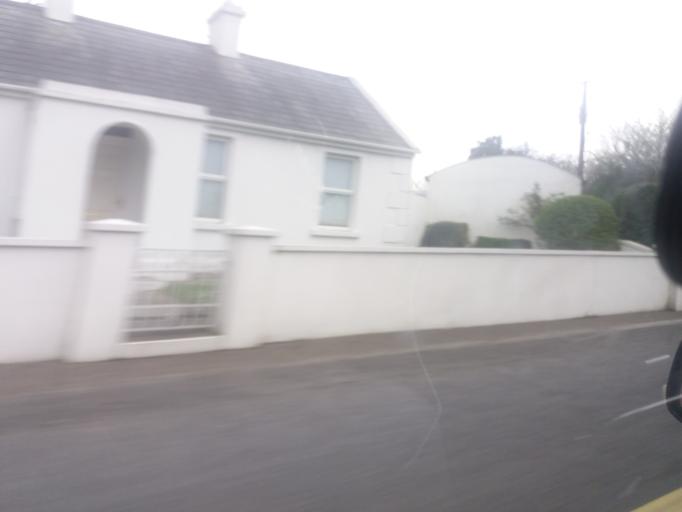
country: IE
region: Munster
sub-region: County Limerick
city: Newcastle West
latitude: 52.4588
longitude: -9.0327
